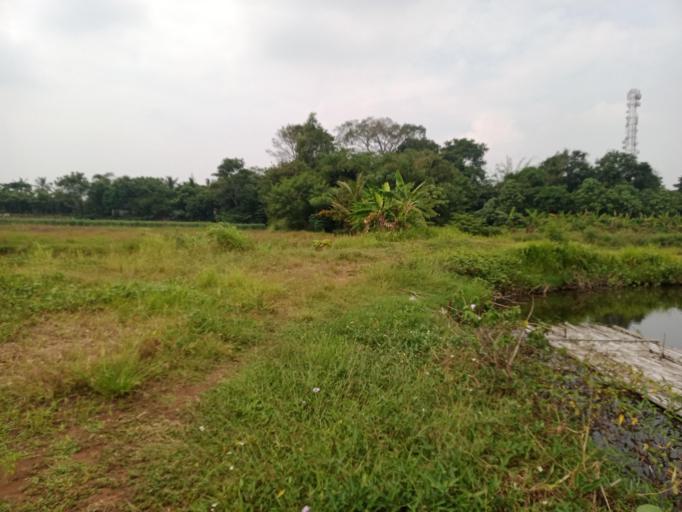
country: ID
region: West Java
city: Kresek
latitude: -6.0941
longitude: 106.4592
